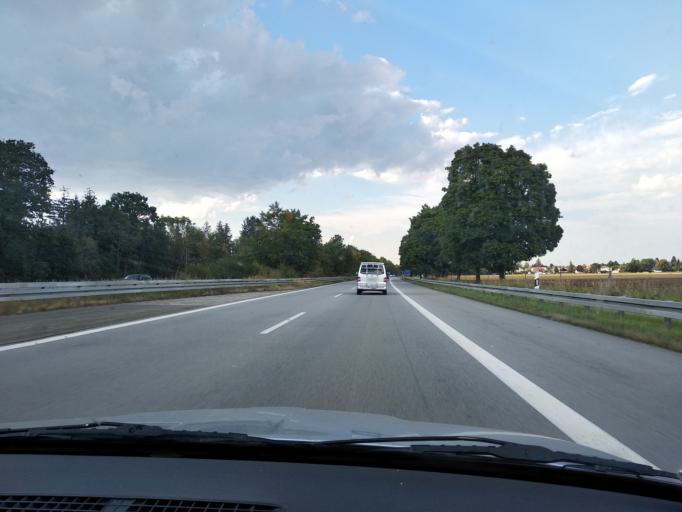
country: DE
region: Bavaria
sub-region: Upper Bavaria
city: Unterhaching
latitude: 48.0614
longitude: 11.5955
